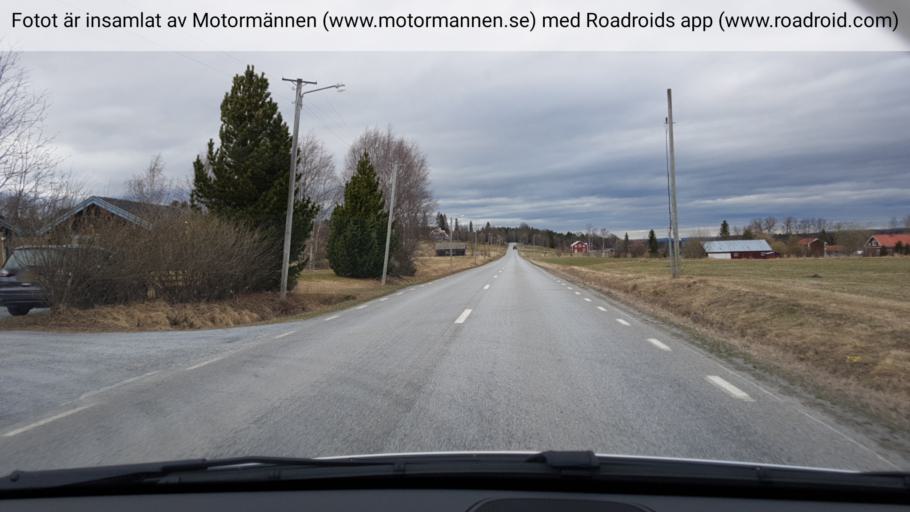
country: SE
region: Jaemtland
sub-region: Krokoms Kommun
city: Krokom
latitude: 63.1456
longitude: 14.1748
